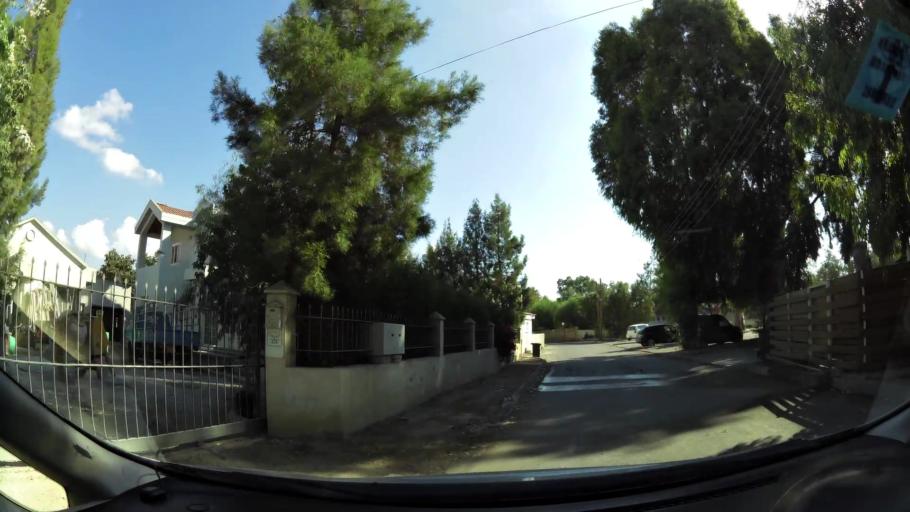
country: CY
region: Lefkosia
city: Nicosia
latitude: 35.2153
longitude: 33.3075
